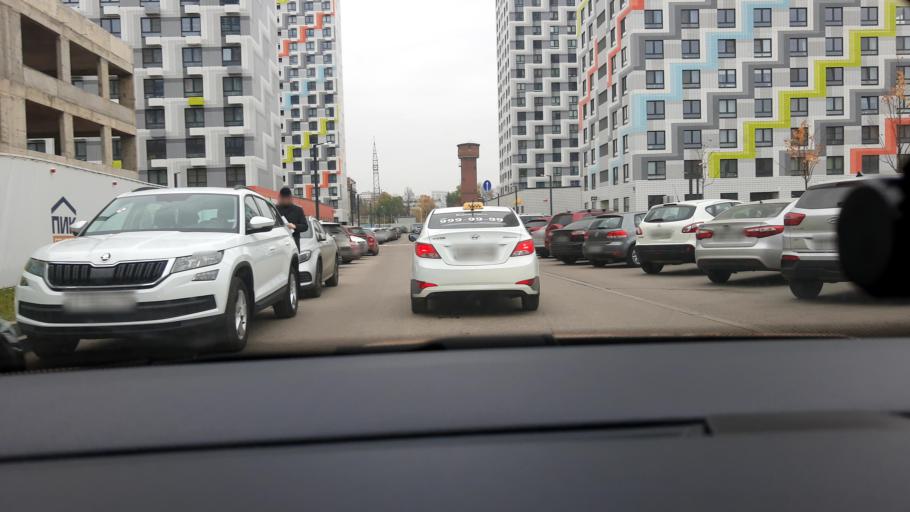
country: RU
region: Moscow
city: Otradnoye
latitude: 55.8748
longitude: 37.6013
